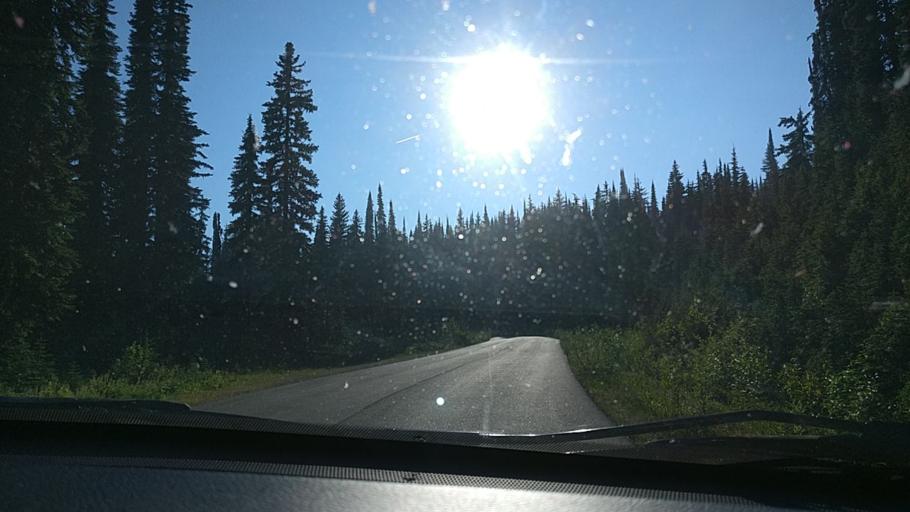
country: CA
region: British Columbia
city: Revelstoke
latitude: 51.0263
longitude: -118.1591
